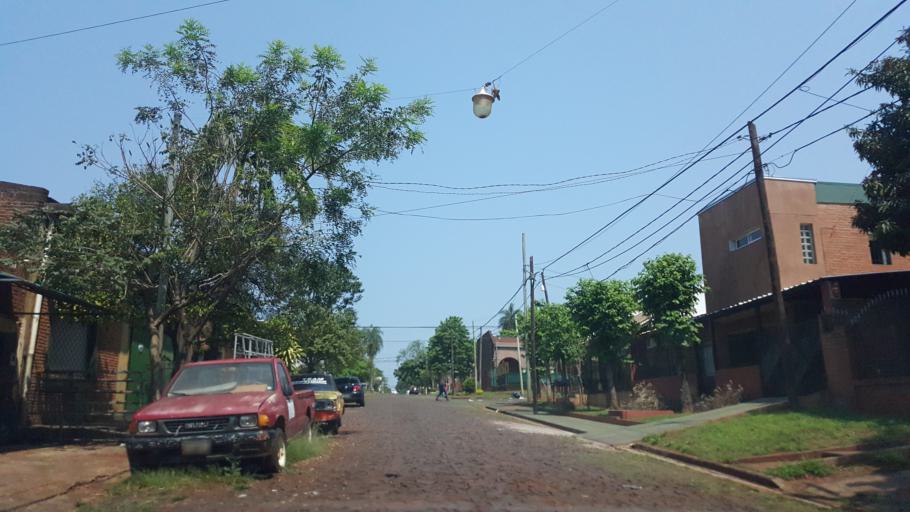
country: AR
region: Misiones
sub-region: Departamento de Capital
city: Posadas
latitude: -27.3839
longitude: -55.9081
